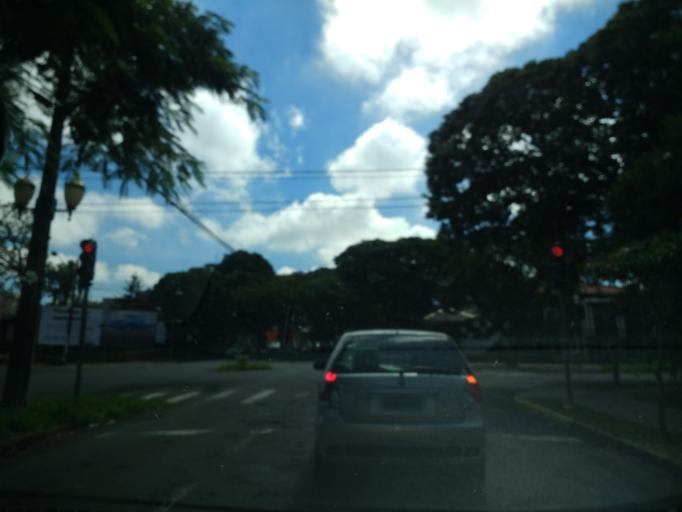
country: BR
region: Parana
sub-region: Umuarama
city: Umuarama
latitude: -23.7614
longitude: -53.3007
